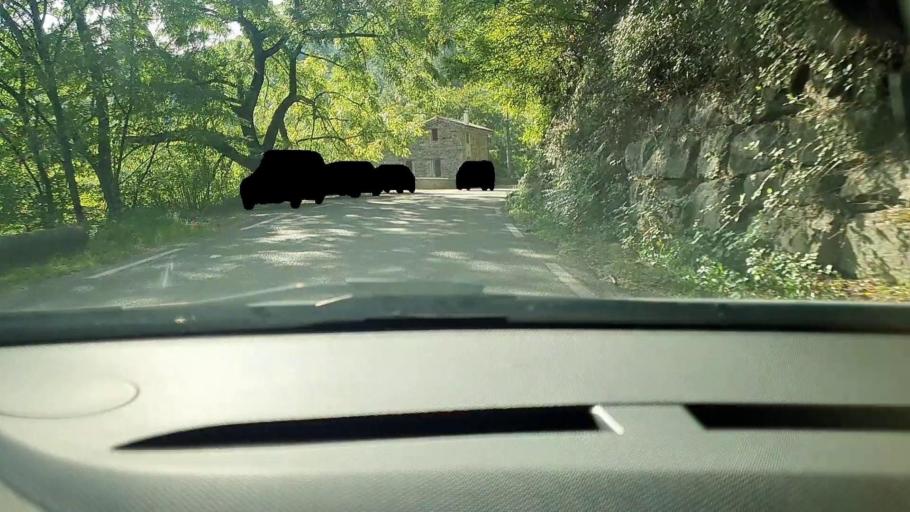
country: FR
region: Languedoc-Roussillon
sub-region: Departement du Gard
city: Besseges
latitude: 44.2911
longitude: 4.0636
